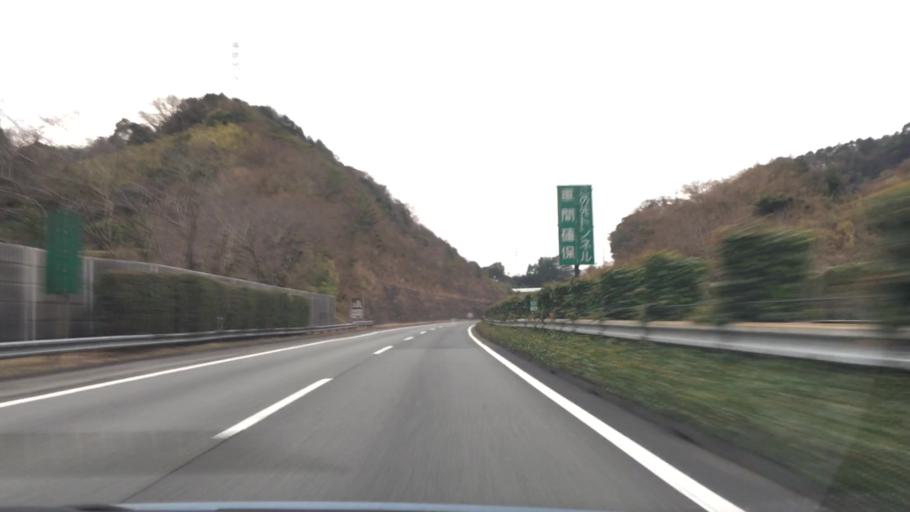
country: JP
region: Shizuoka
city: Fuji
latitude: 35.1324
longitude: 138.6144
